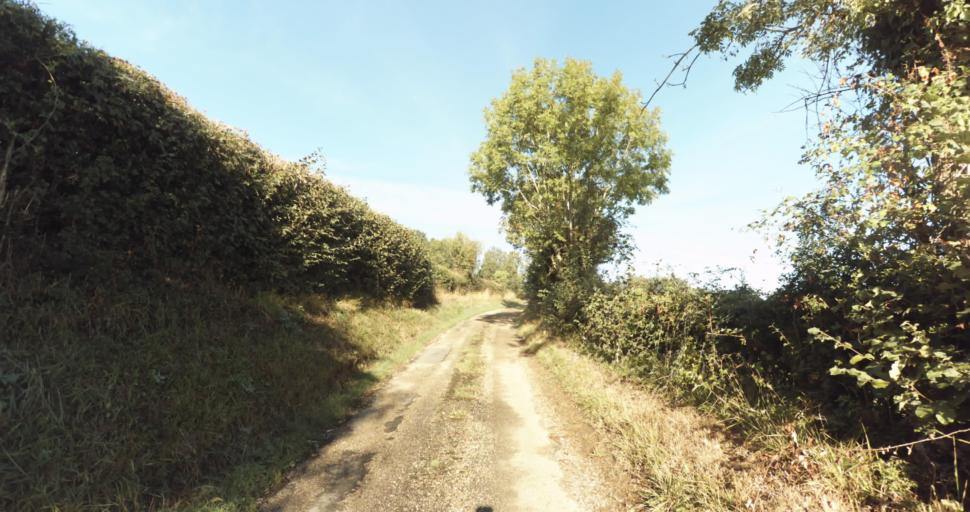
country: FR
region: Lower Normandy
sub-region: Departement de l'Orne
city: Vimoutiers
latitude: 48.9168
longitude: 0.1797
